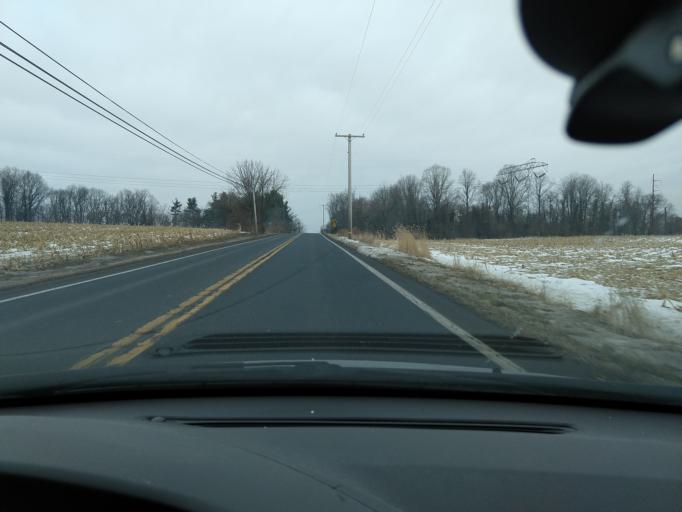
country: US
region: Pennsylvania
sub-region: Lehigh County
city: Macungie
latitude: 40.4736
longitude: -75.5354
